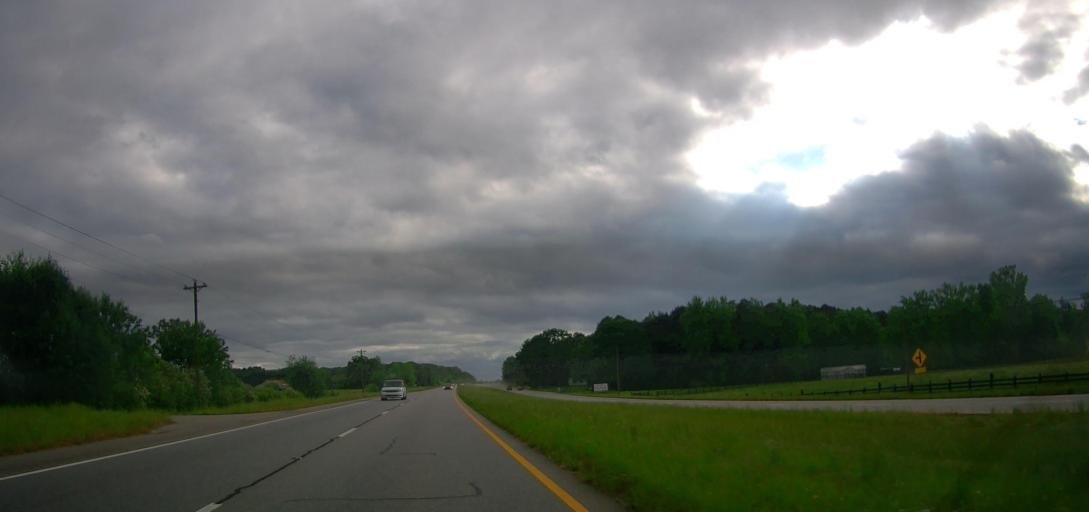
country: US
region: Georgia
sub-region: Barrow County
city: Statham
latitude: 33.8553
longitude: -83.6146
